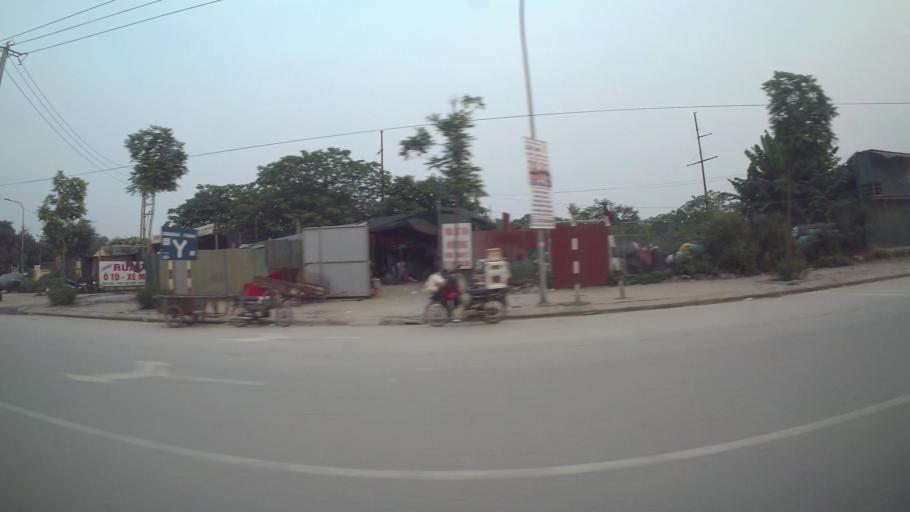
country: VN
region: Ha Noi
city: Thanh Xuan
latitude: 20.9788
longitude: 105.8068
